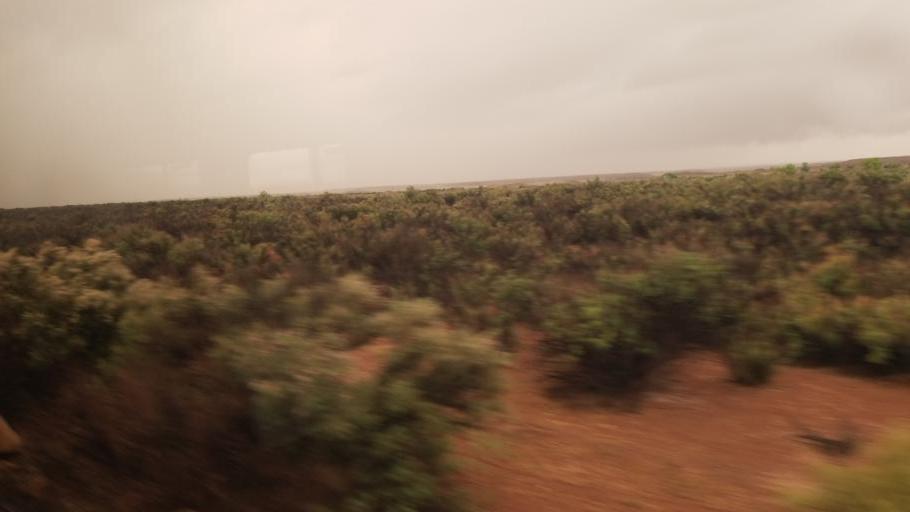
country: US
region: Arizona
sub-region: Navajo County
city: Joseph City
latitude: 34.9590
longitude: -110.3776
